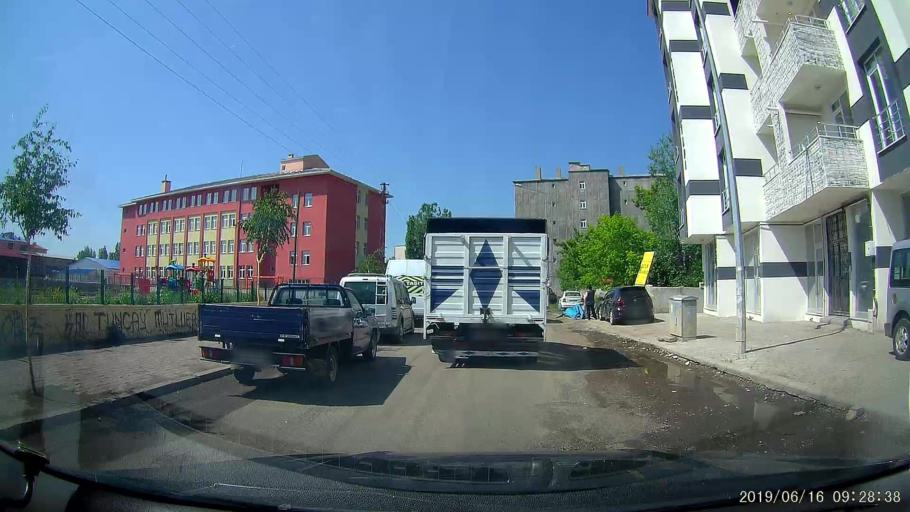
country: TR
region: Kars
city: Kars
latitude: 40.6027
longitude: 43.1036
